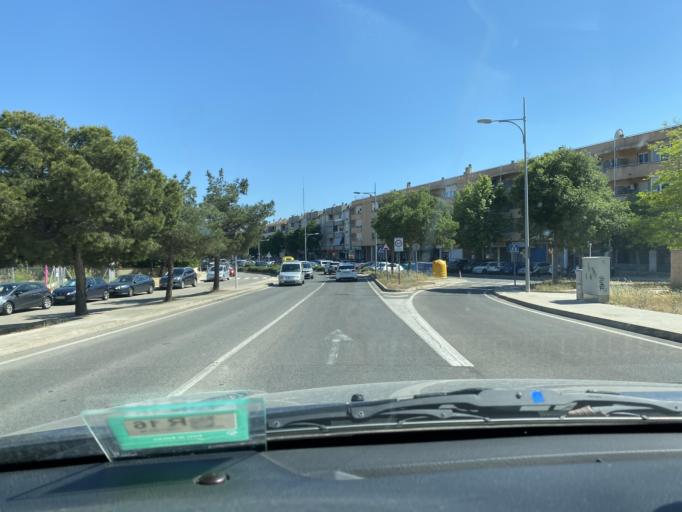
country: ES
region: Balearic Islands
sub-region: Illes Balears
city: Palma
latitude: 39.6052
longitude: 2.6862
